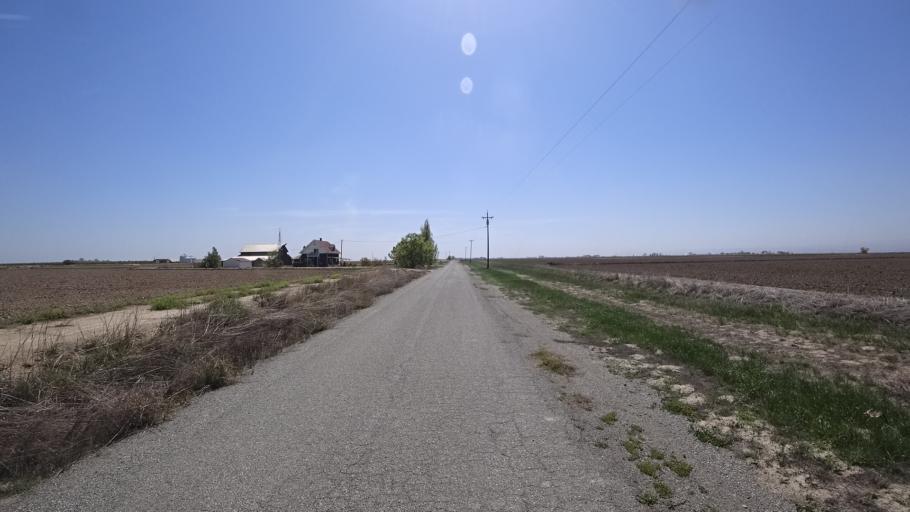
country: US
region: California
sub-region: Glenn County
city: Willows
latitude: 39.5189
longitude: -122.1169
